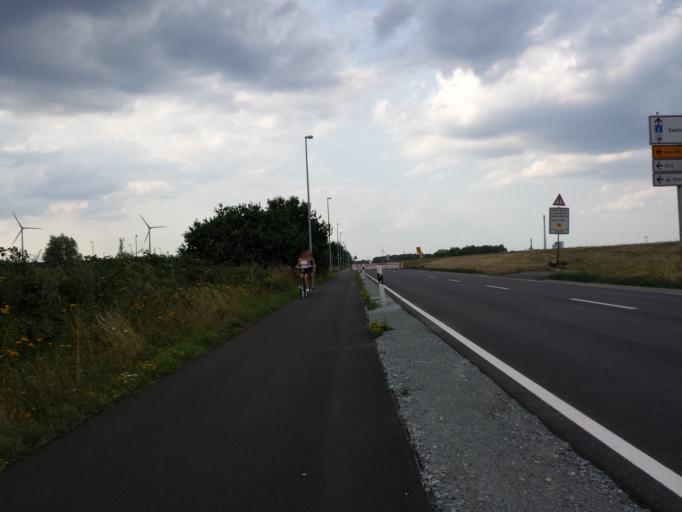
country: DE
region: Lower Saxony
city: Stuhr
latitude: 53.0904
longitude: 8.7319
